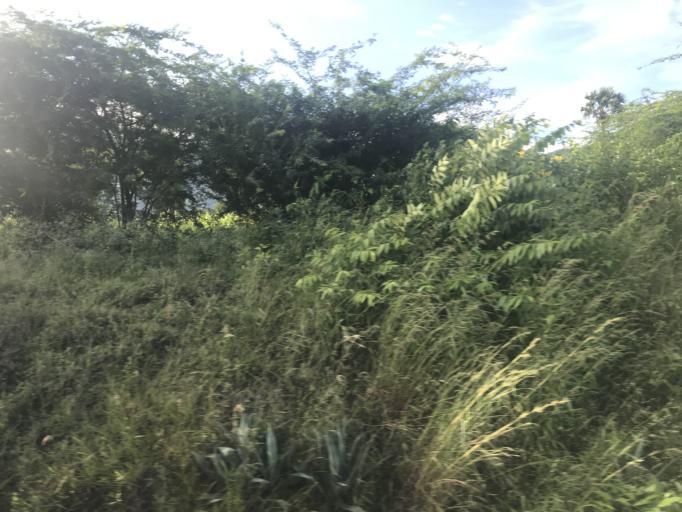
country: IN
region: Tamil Nadu
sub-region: Coimbatore
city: Madukkarai
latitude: 10.8895
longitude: 76.8797
